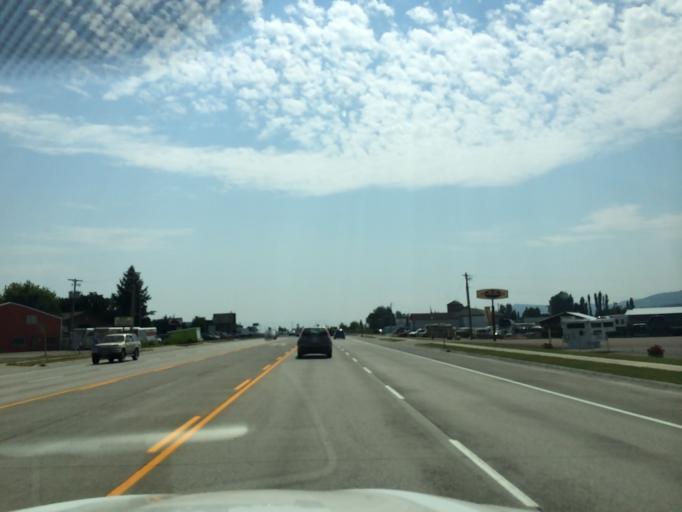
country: US
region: Montana
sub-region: Flathead County
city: Kalispell
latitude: 48.1697
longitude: -114.2930
